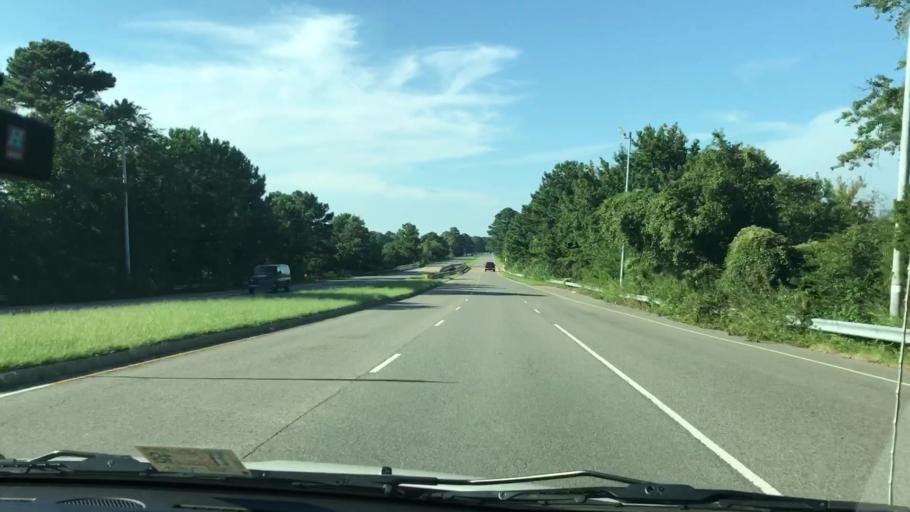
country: US
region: Virginia
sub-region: City of Hampton
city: Hampton
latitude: 37.0454
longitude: -76.3638
